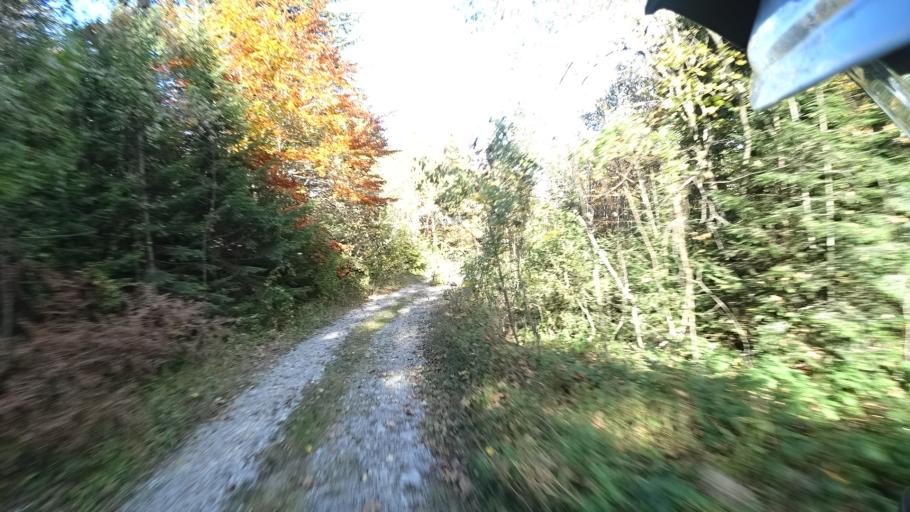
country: HR
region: Karlovacka
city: Plaski
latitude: 45.0665
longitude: 15.3209
